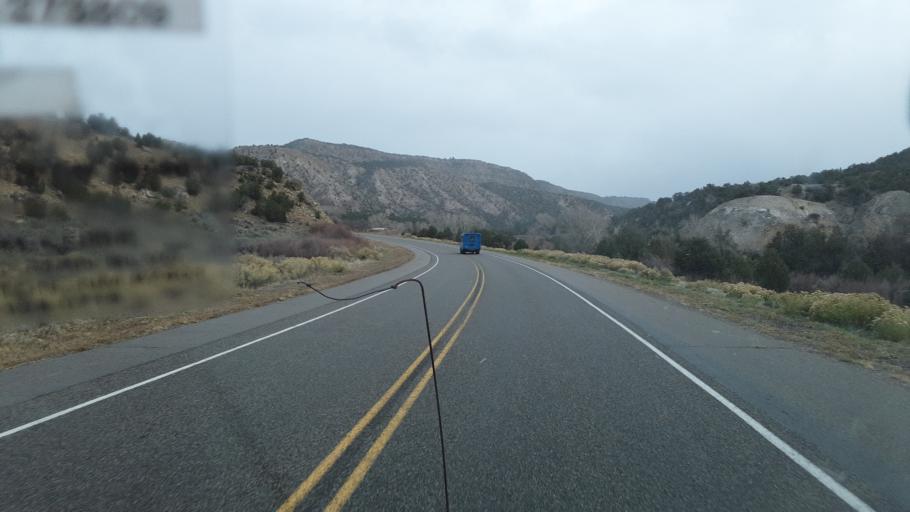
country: US
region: New Mexico
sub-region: Rio Arriba County
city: Santa Teresa
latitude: 36.3873
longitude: -106.4946
